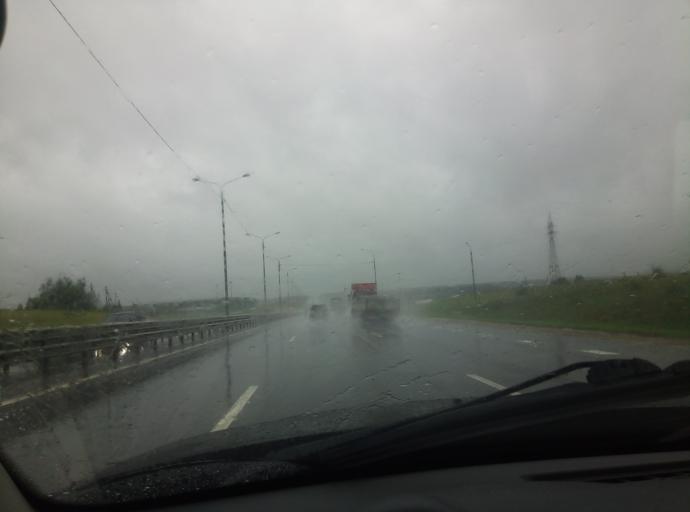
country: RU
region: Moskovskaya
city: Melikhovo
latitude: 55.1270
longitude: 37.5690
